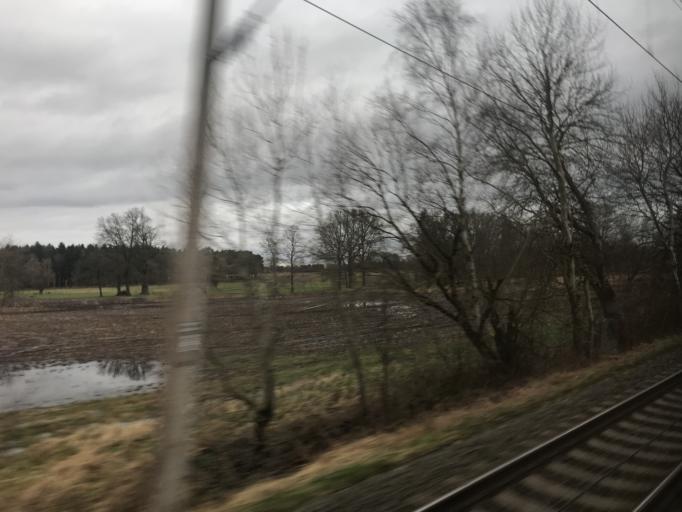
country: DE
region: Lower Saxony
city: Edemissen
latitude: 52.4381
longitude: 10.2622
